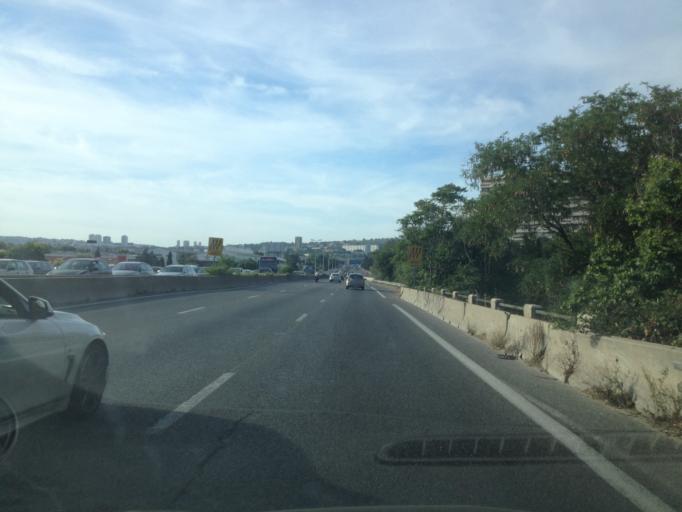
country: FR
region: Provence-Alpes-Cote d'Azur
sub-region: Departement des Bouches-du-Rhone
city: Marseille 14
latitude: 43.3303
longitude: 5.3779
